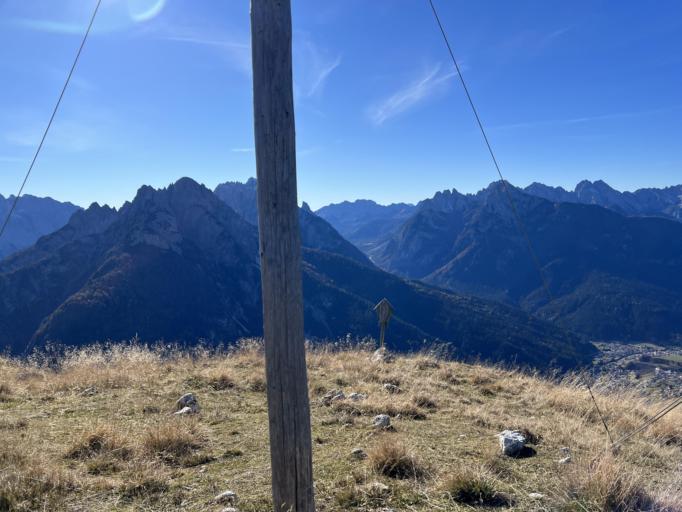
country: IT
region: Veneto
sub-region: Provincia di Belluno
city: San Pietro di Cadore
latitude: 46.5956
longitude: 12.6130
